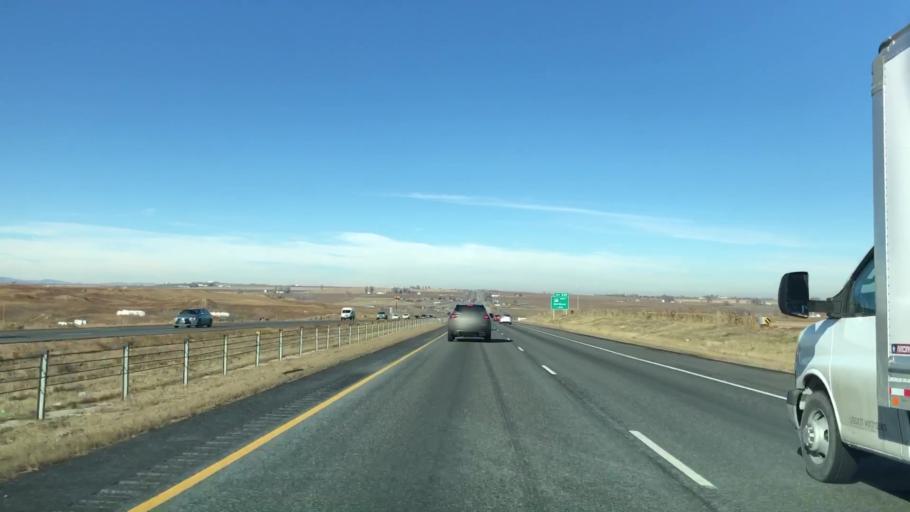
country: US
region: Colorado
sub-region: Weld County
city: Mead
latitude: 40.2889
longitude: -104.9815
